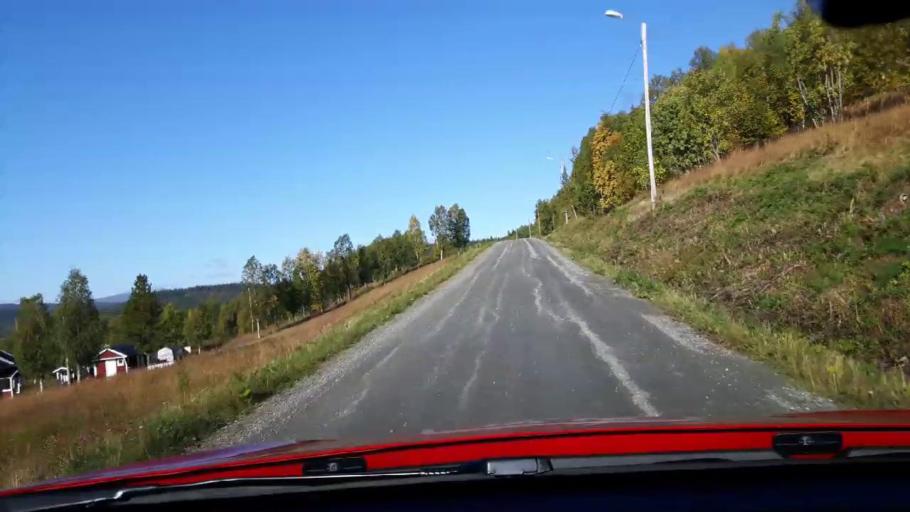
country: NO
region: Nord-Trondelag
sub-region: Lierne
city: Sandvika
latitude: 64.6056
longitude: 13.7815
